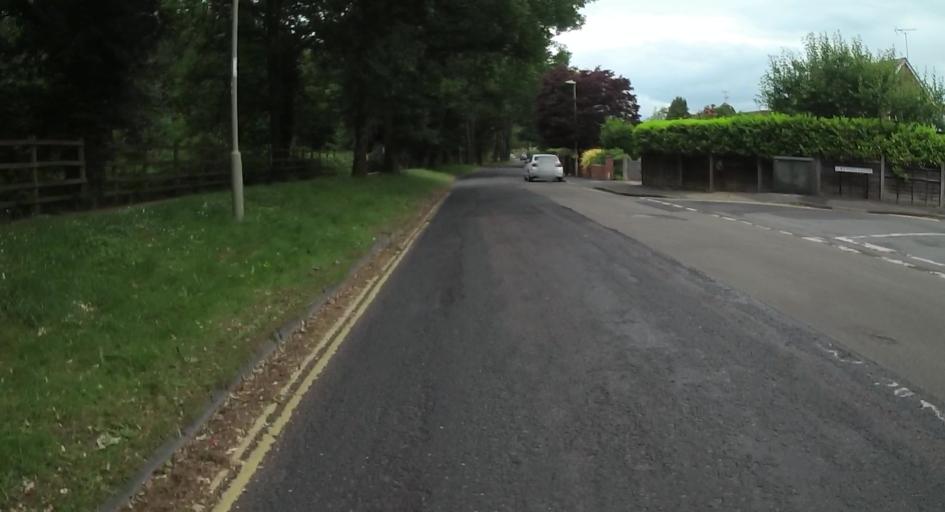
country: GB
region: England
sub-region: Hampshire
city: Fleet
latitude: 51.2585
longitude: -0.8325
